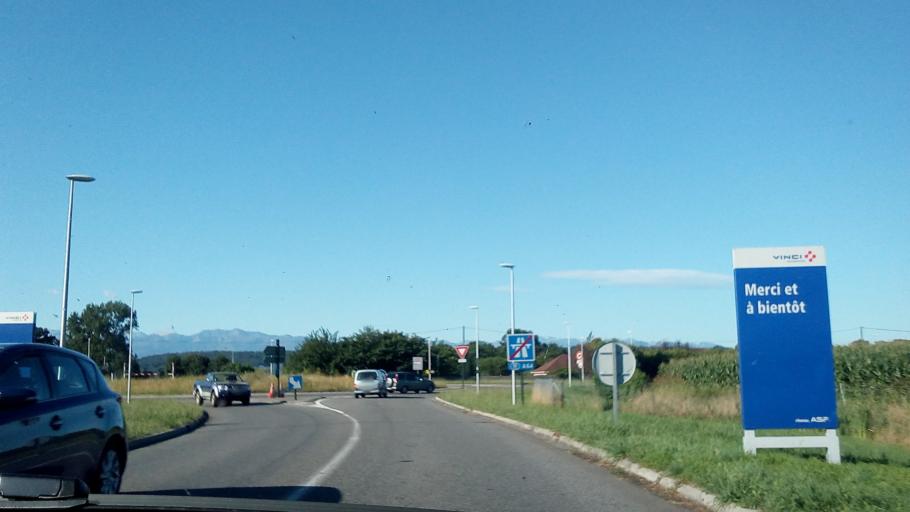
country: FR
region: Aquitaine
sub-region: Departement des Pyrenees-Atlantiques
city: Nousty
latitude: 43.2713
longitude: -0.2016
